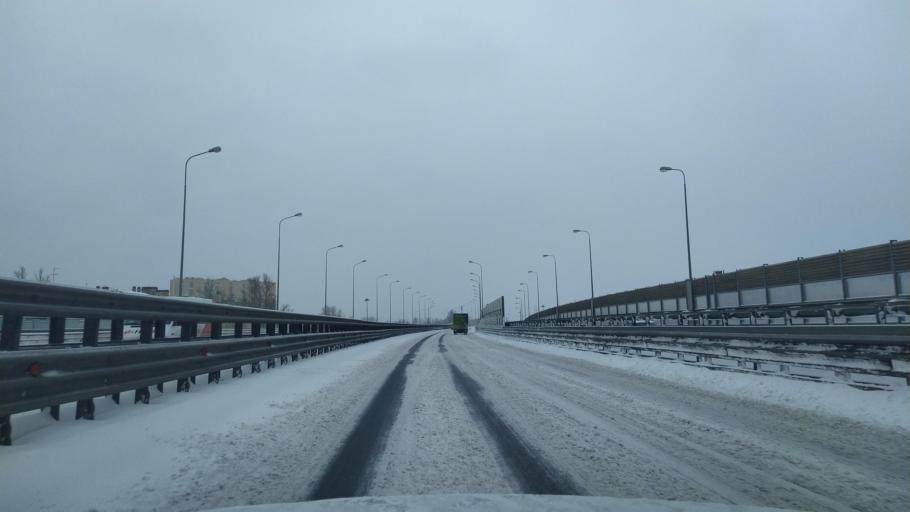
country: RU
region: St.-Petersburg
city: Krasnogvargeisky
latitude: 59.9840
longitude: 30.5143
